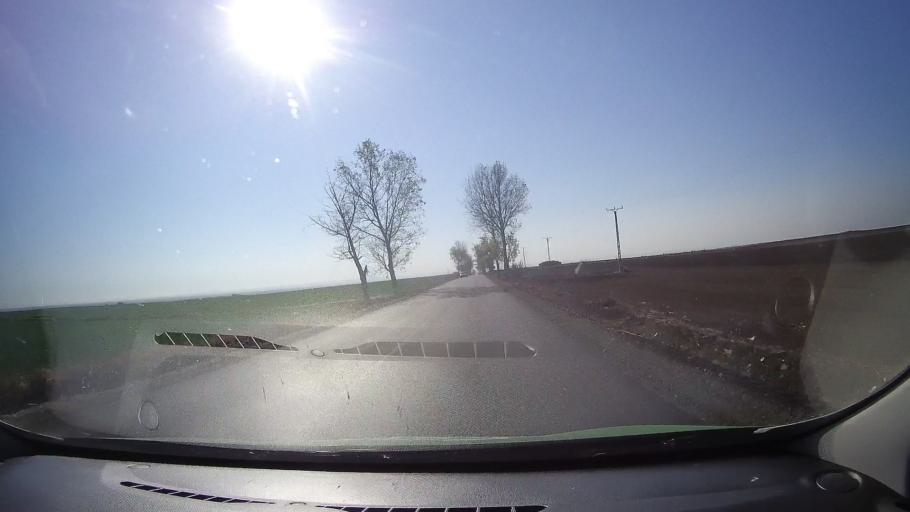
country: RO
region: Satu Mare
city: Carei
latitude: 47.6553
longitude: 22.4609
